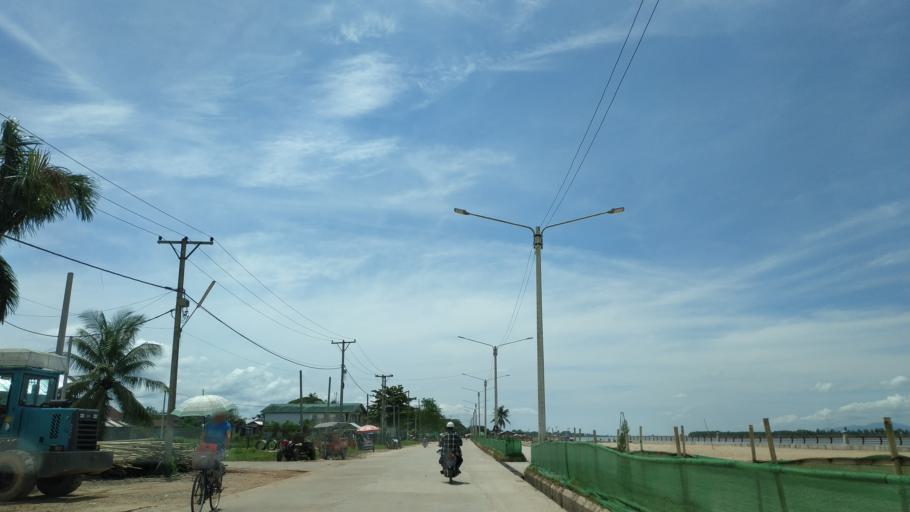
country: MM
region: Tanintharyi
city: Dawei
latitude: 14.0755
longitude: 98.1838
